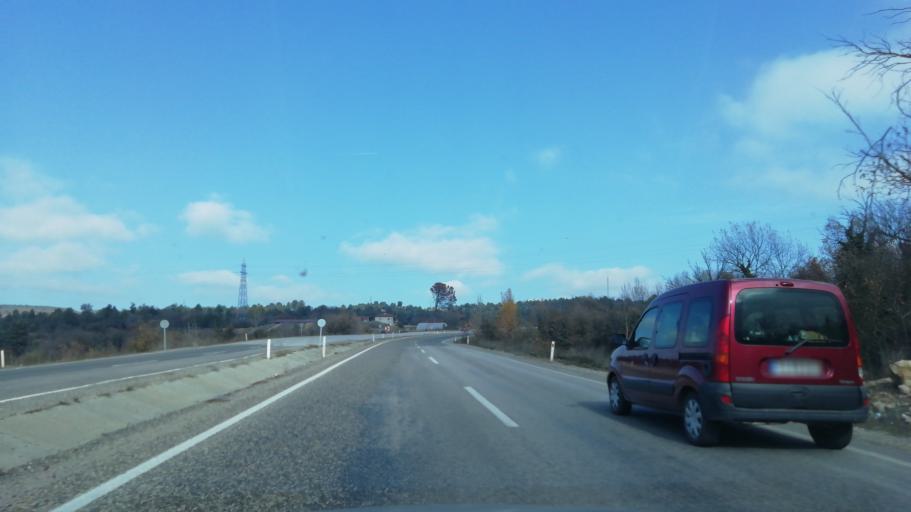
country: TR
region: Karabuk
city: Safranbolu
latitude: 41.2214
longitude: 32.7676
